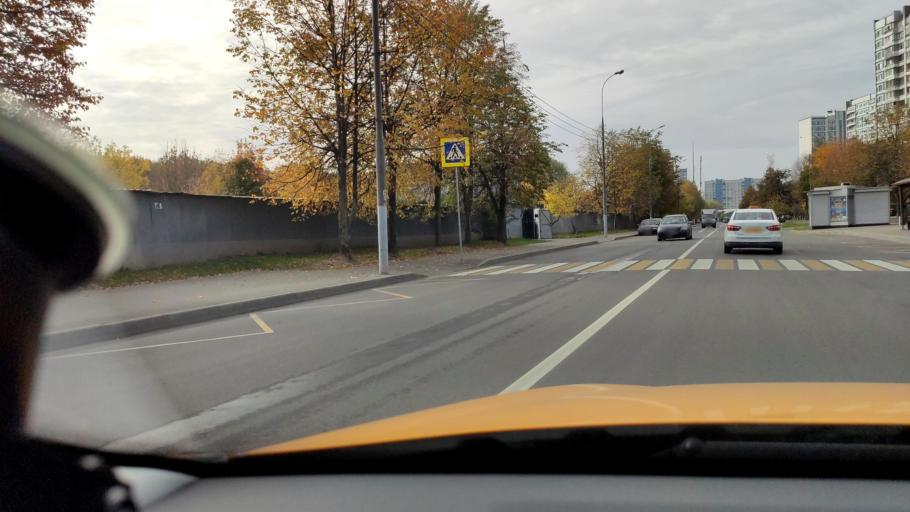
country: RU
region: Moscow
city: Zyablikovo
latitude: 55.6067
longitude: 37.7532
